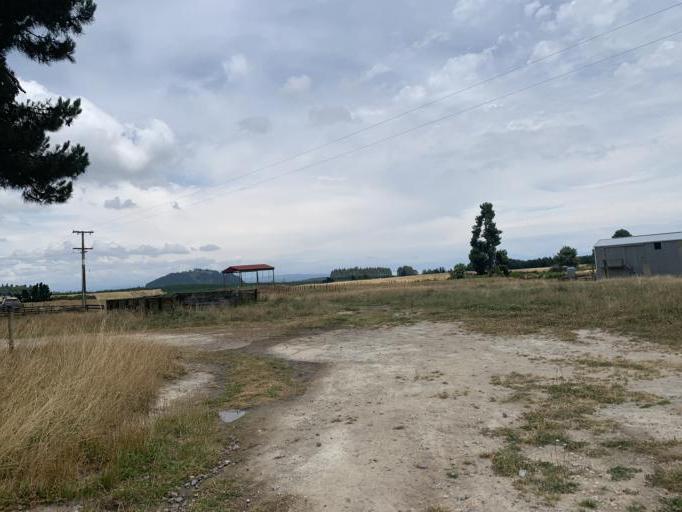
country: NZ
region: Waikato
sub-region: Taupo District
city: Taupo
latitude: -38.7043
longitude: 176.1402
